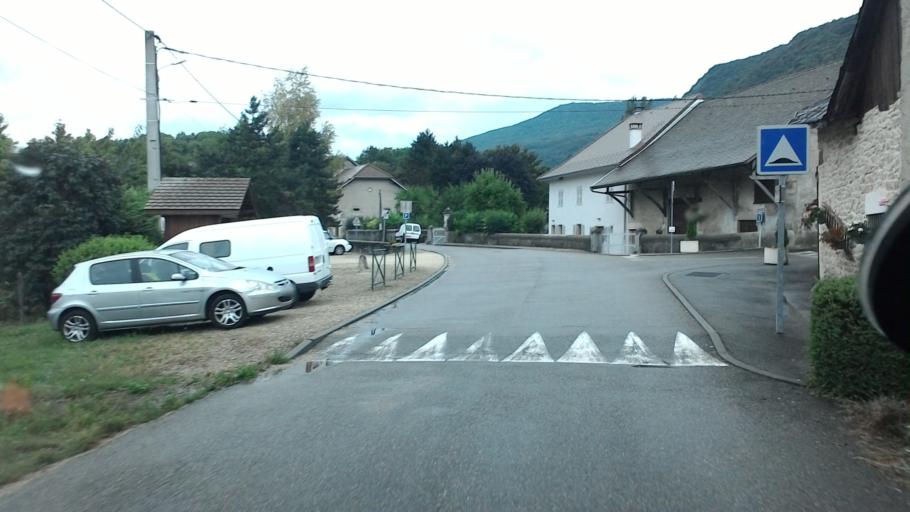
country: FR
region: Rhone-Alpes
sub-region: Departement de l'Ain
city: Belley
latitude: 45.7659
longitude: 5.6100
